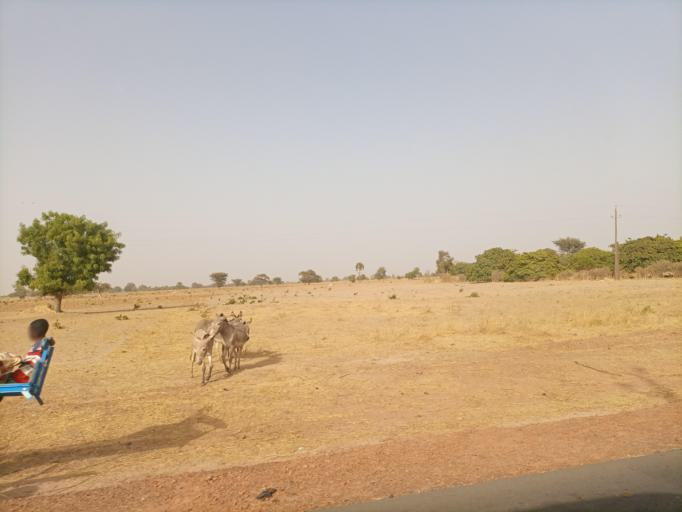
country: SN
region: Fatick
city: Passi
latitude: 14.0416
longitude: -16.3220
